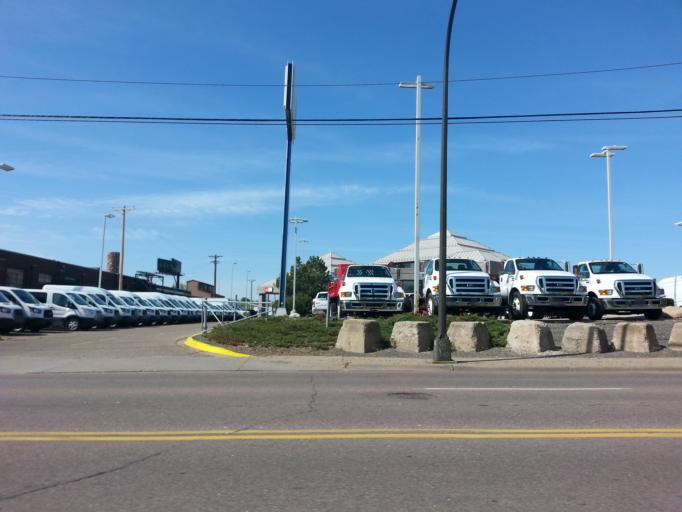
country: US
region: Minnesota
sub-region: Ramsey County
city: Lauderdale
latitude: 44.9987
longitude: -93.2258
